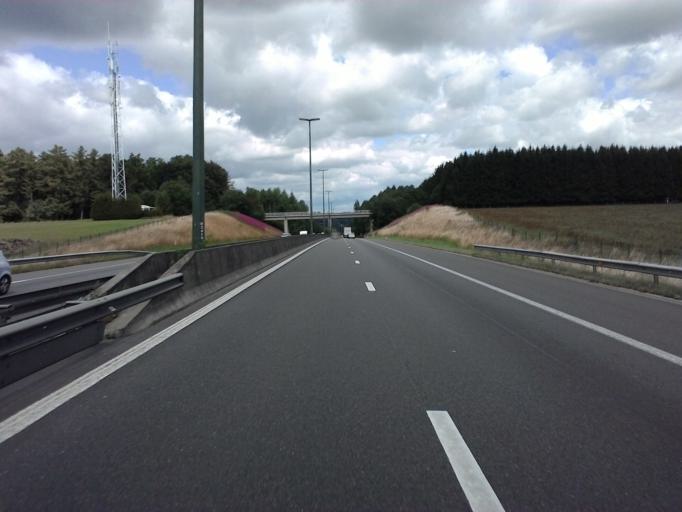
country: BE
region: Wallonia
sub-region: Province du Luxembourg
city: Leglise
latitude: 49.7832
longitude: 5.5362
